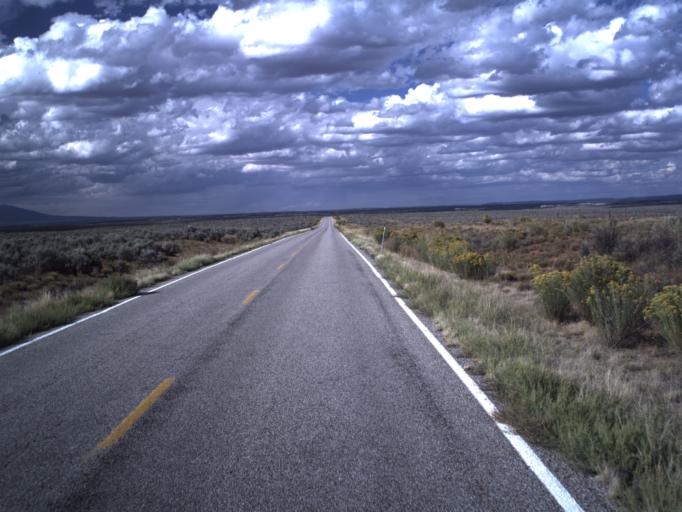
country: US
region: Utah
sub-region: San Juan County
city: Blanding
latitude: 37.3746
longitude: -109.3426
